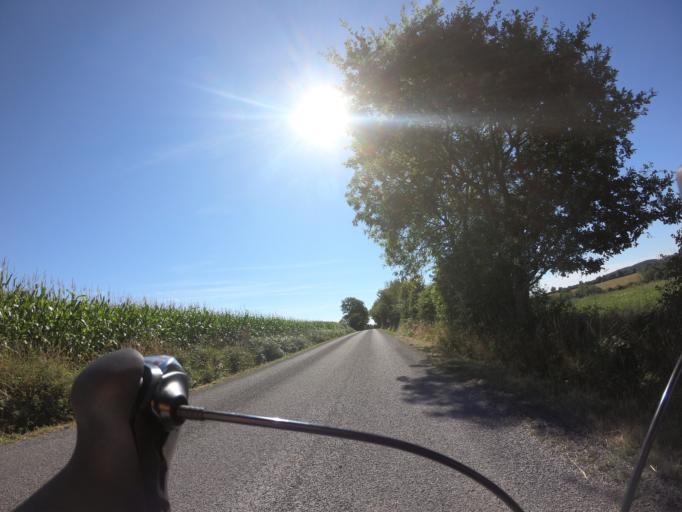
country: FR
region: Pays de la Loire
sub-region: Departement de la Mayenne
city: Pre-en-Pail
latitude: 48.5576
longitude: -0.1250
